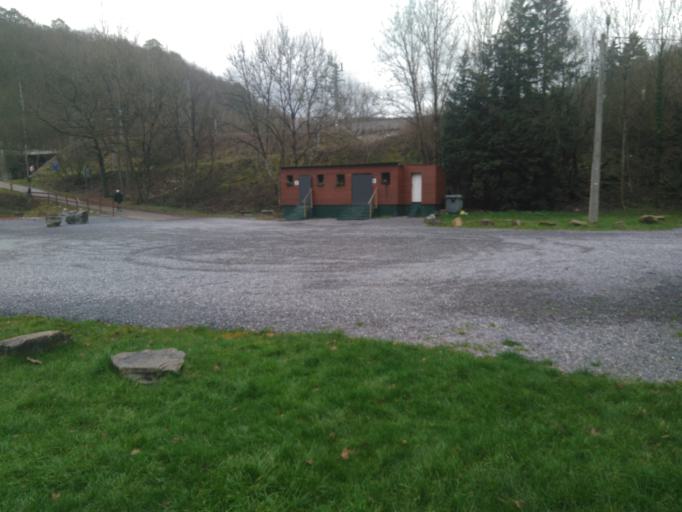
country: BE
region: Wallonia
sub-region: Province de Namur
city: Houyet
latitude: 50.2107
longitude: 4.9637
